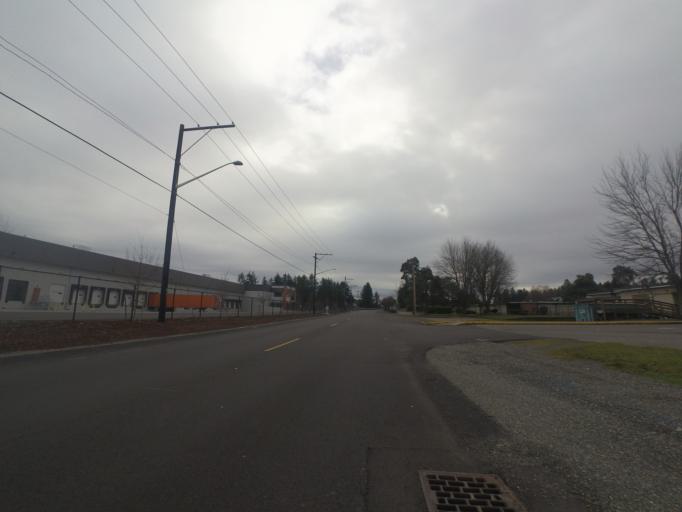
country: US
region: Washington
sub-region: Pierce County
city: Fort Lewis
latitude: 47.1227
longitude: -122.5375
